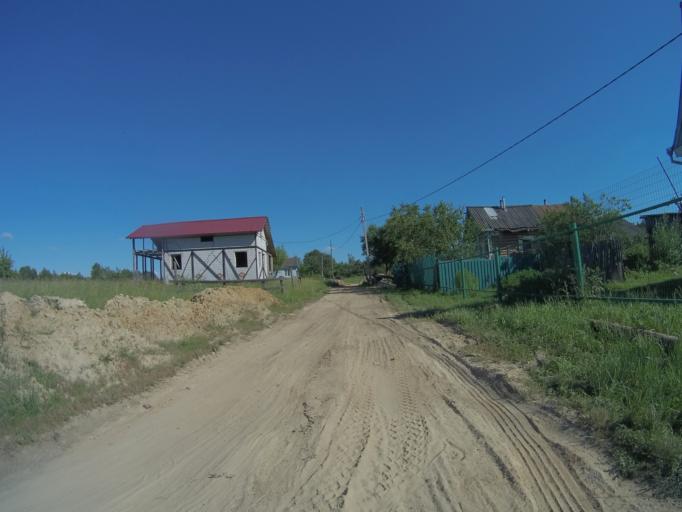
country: RU
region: Vladimir
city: Raduzhnyy
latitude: 56.0046
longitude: 40.3930
